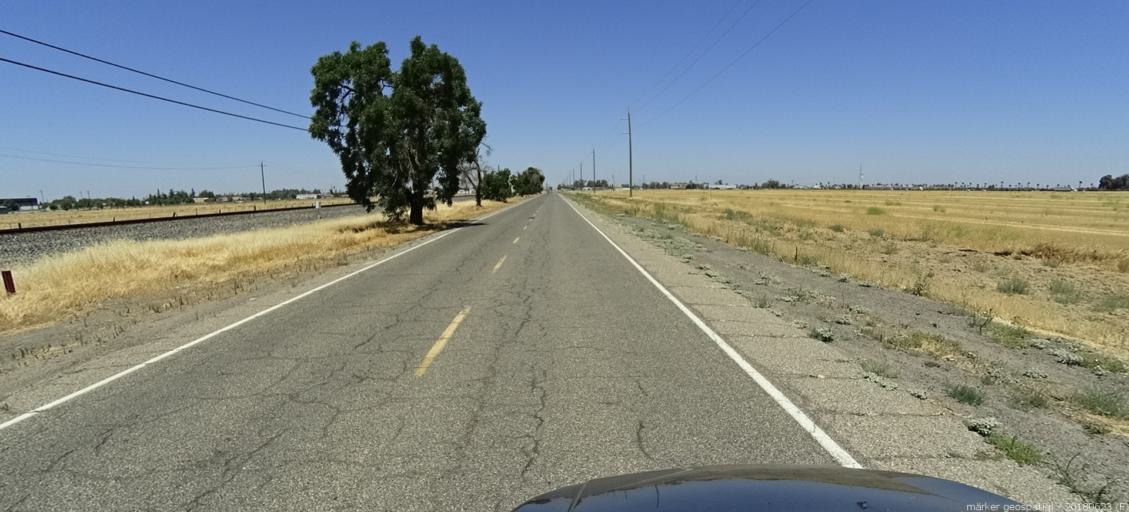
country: US
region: California
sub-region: Madera County
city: Chowchilla
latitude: 37.1143
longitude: -120.2439
